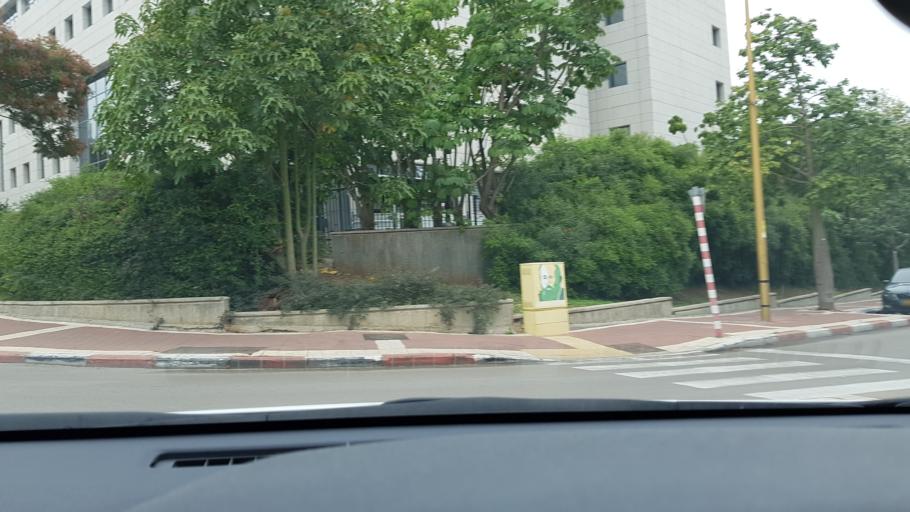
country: IL
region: Central District
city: Ness Ziona
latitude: 31.9111
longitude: 34.8088
